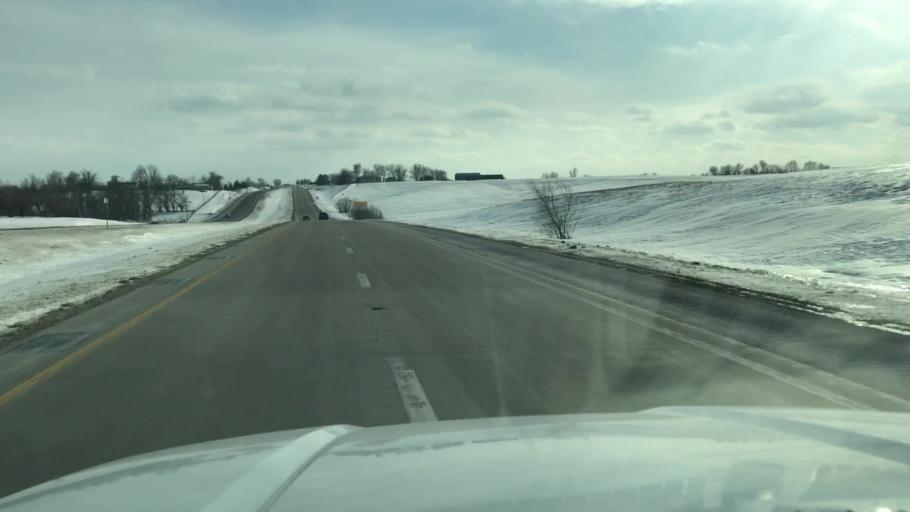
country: US
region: Missouri
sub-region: Nodaway County
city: Maryville
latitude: 40.2987
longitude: -94.8752
